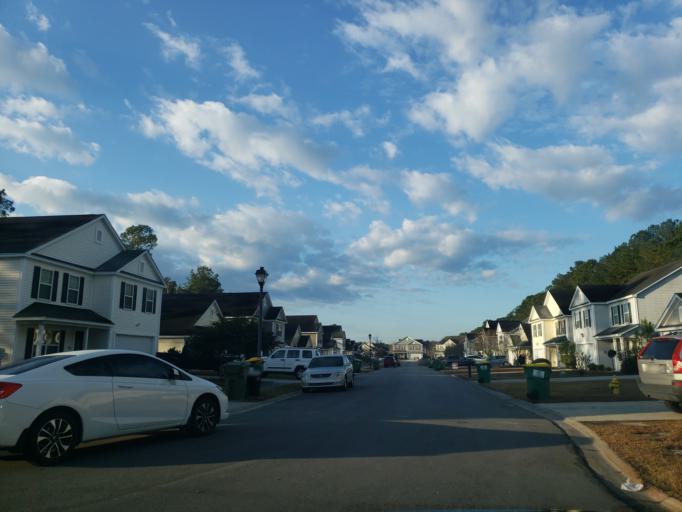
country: US
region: Georgia
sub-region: Chatham County
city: Bloomingdale
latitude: 32.1580
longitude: -81.2670
